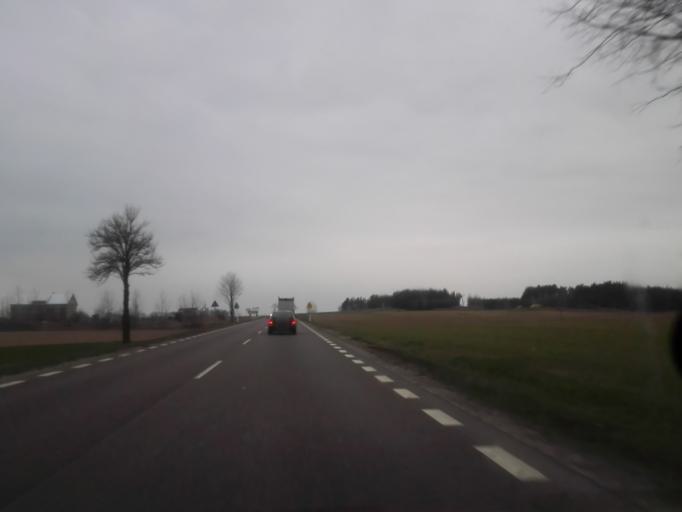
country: PL
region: Podlasie
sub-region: Powiat grajewski
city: Grajewo
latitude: 53.6181
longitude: 22.3920
